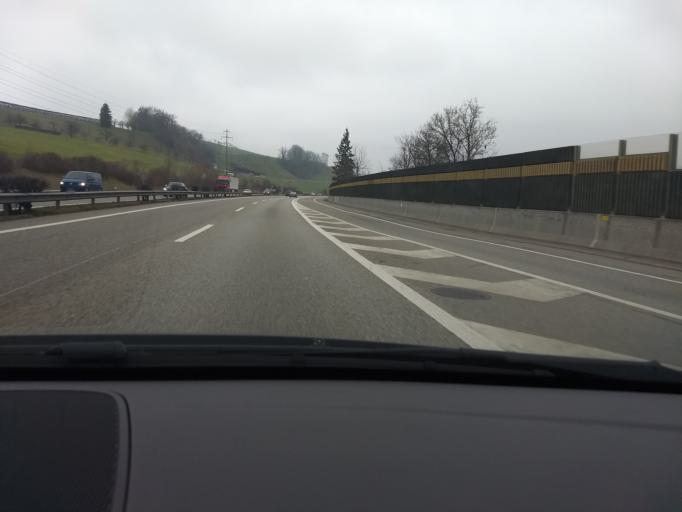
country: CH
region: Basel-Landschaft
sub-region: Bezirk Waldenburg
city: Diegten
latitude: 47.4049
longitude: 7.8070
